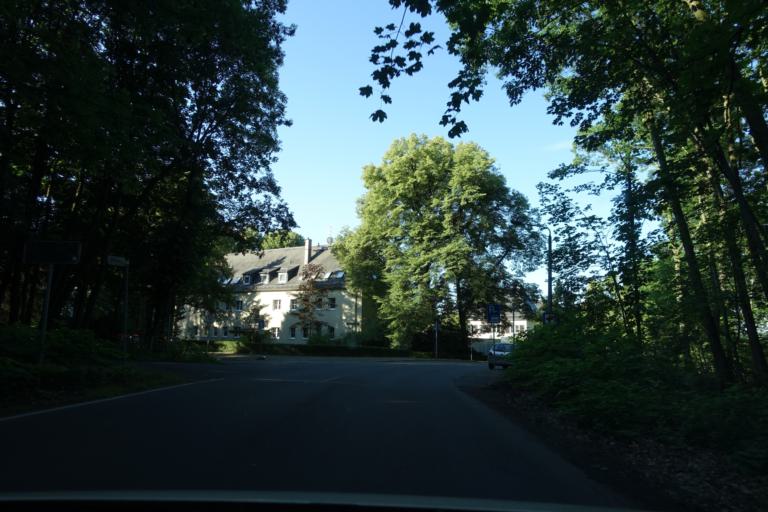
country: DE
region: Saxony
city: Hilbersdorf
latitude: 50.8414
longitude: 12.9656
